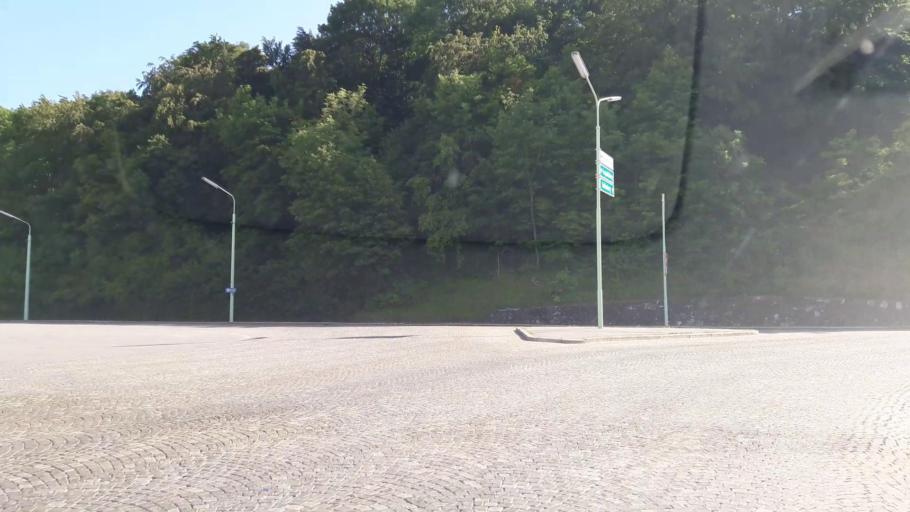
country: AT
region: Lower Austria
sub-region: Politischer Bezirk Korneuburg
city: Langenzersdorf
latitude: 48.2773
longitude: 16.3351
